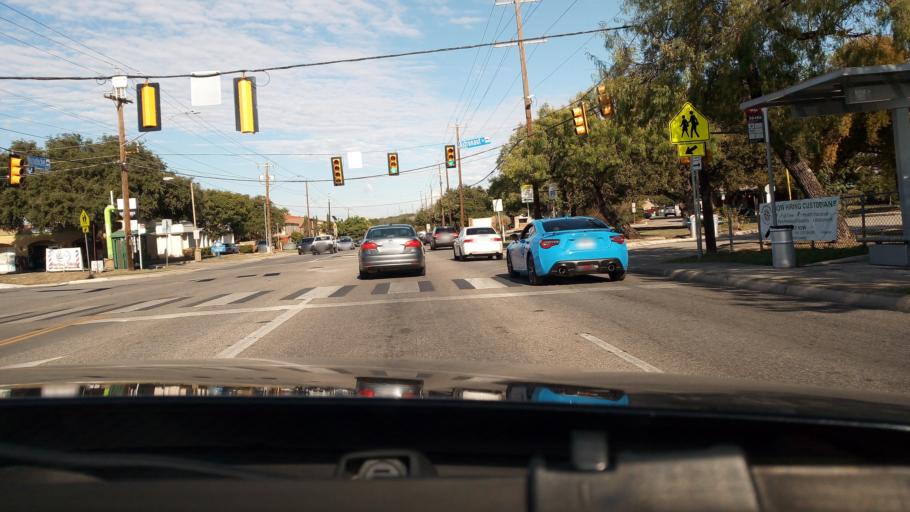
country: US
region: Texas
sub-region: Bexar County
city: Alamo Heights
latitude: 29.5269
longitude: -98.4374
